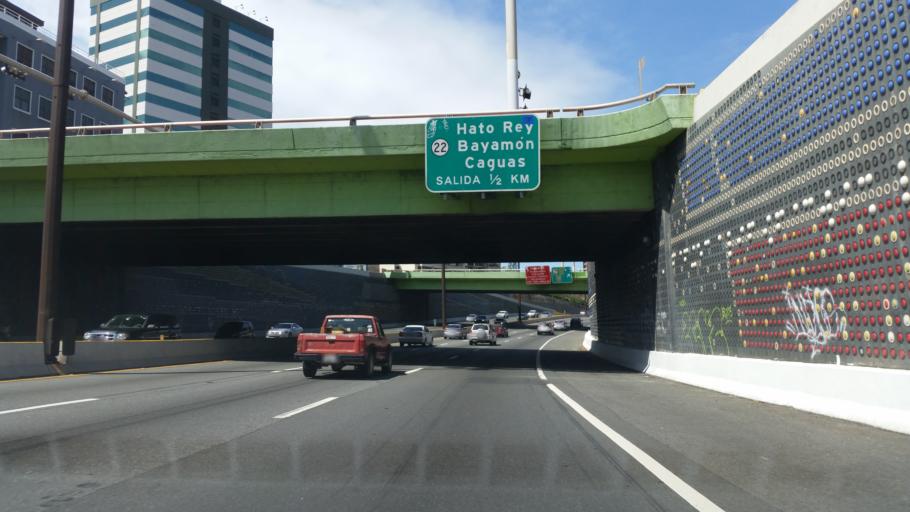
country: PR
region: San Juan
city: San Juan
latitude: 18.4484
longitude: -66.0623
